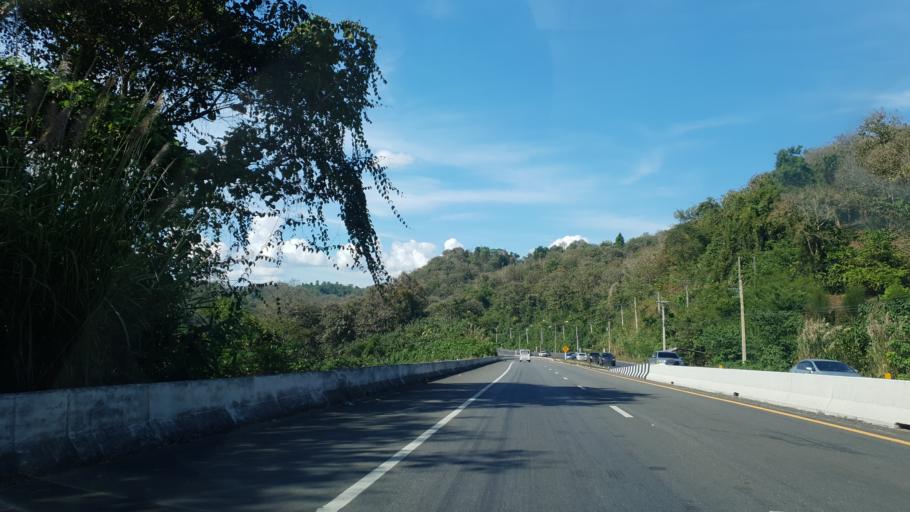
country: TH
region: Phrae
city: Den Chai
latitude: 17.8603
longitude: 100.0446
